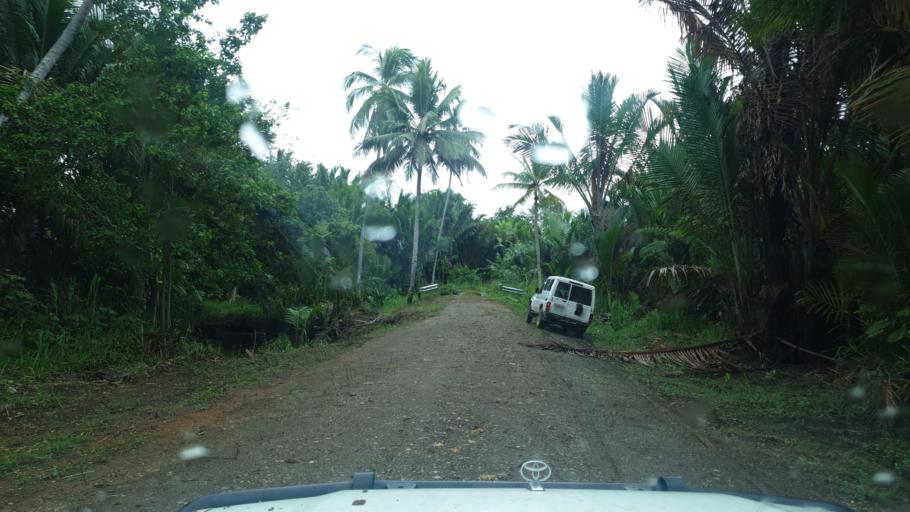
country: PG
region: Gulf
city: Kerema
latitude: -7.9543
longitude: 145.8390
